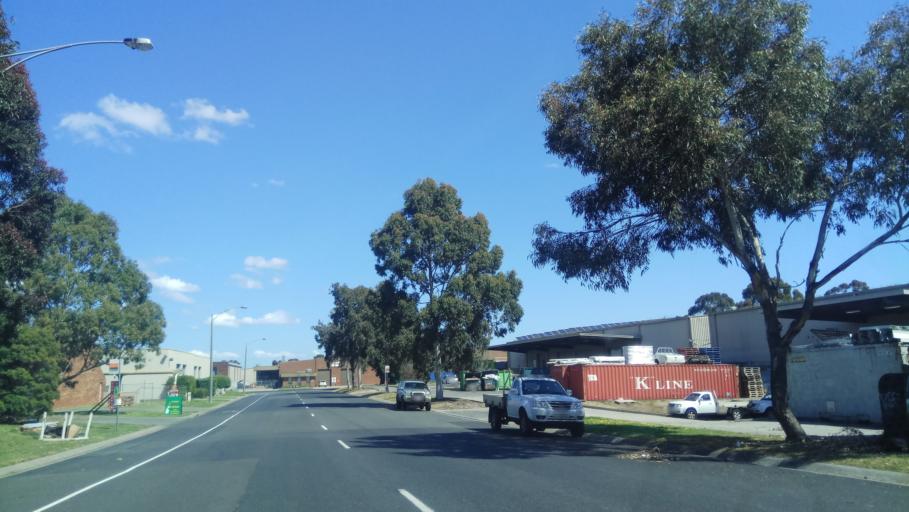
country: AU
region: Victoria
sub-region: Kingston
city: Dingley Village
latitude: -37.9827
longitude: 145.1137
